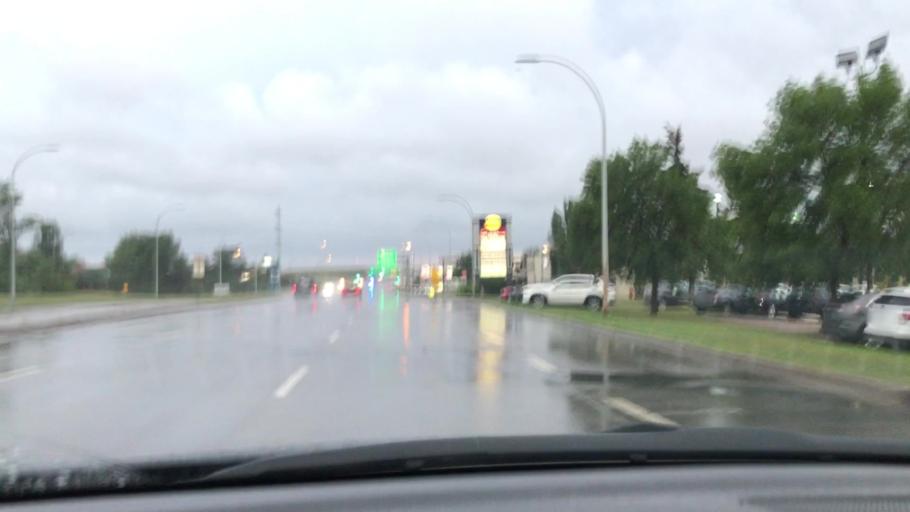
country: CA
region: Alberta
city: Sherwood Park
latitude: 53.5122
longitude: -113.3259
